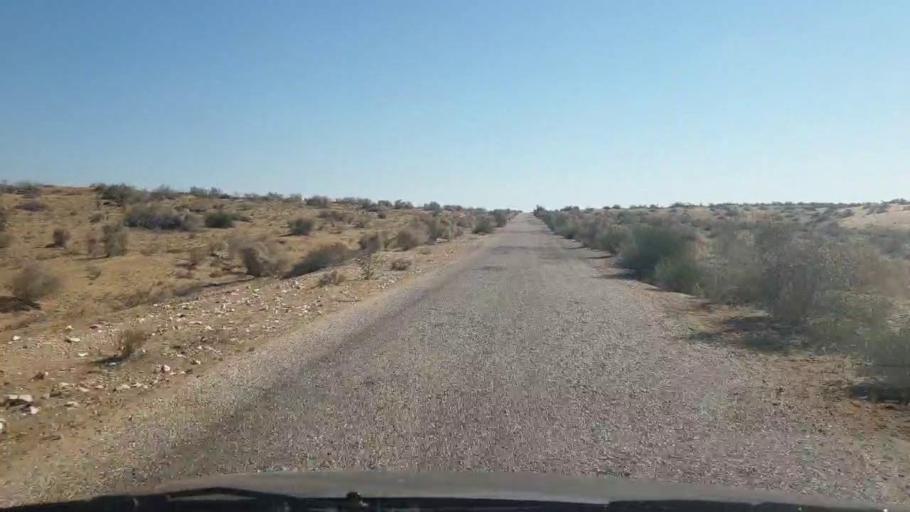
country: PK
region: Sindh
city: Bozdar
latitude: 27.0042
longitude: 68.8048
